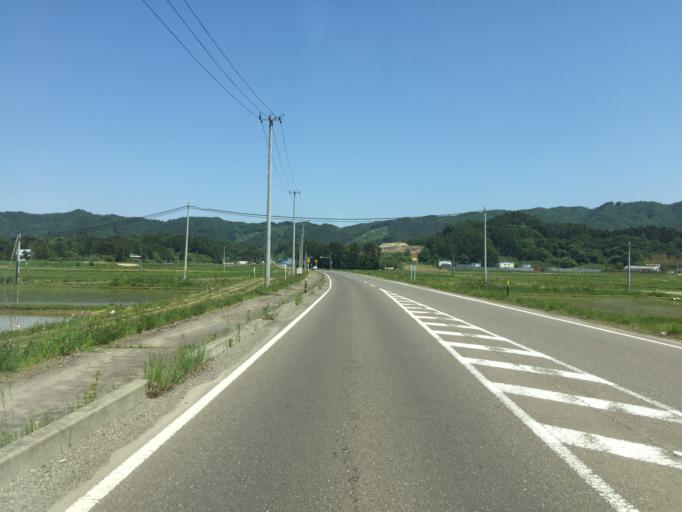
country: JP
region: Miyagi
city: Kakuda
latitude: 37.9681
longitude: 140.8242
